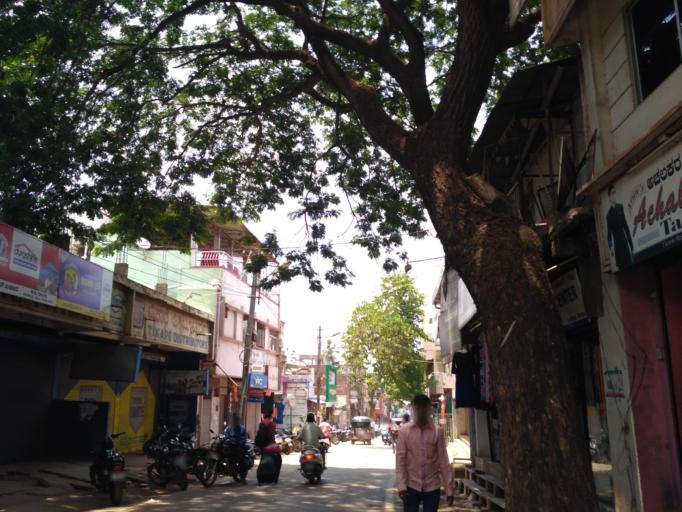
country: IN
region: Karnataka
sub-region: Dharwad
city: Hubli
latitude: 15.4569
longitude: 75.0115
